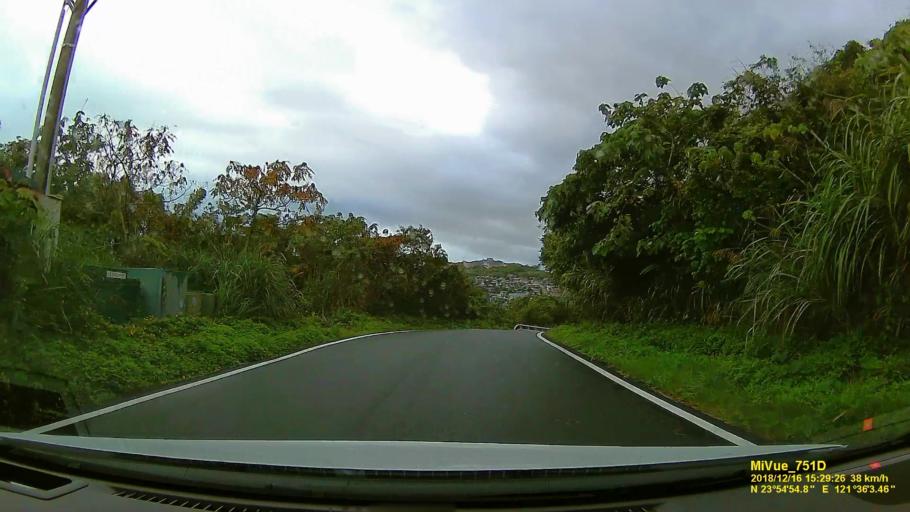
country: TW
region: Taiwan
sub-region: Hualien
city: Hualian
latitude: 23.9150
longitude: 121.6008
